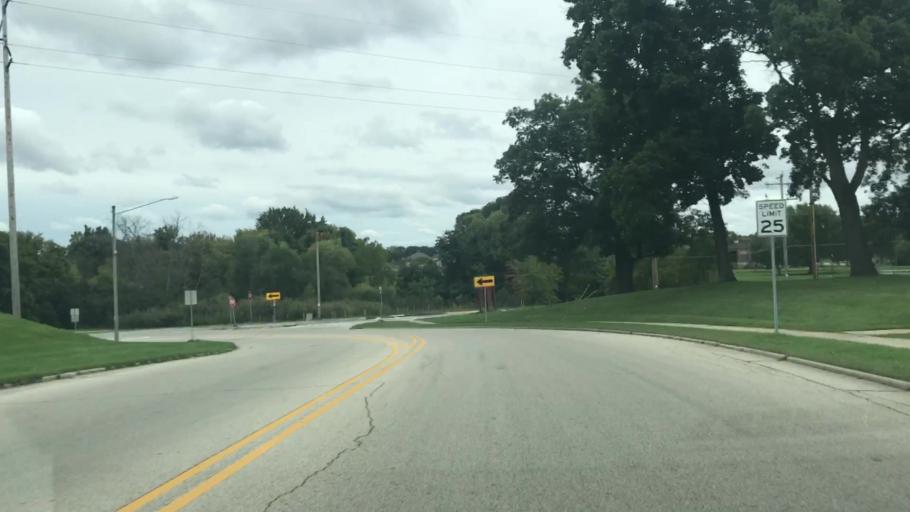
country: US
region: Wisconsin
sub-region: Waukesha County
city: Mukwonago
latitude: 42.8579
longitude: -88.3293
